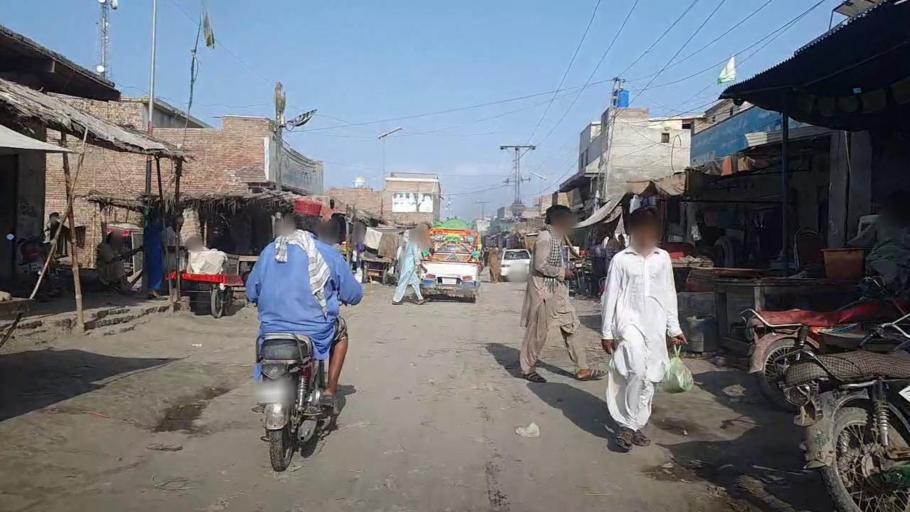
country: PK
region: Sindh
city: Khairpur
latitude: 28.0774
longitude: 69.7927
